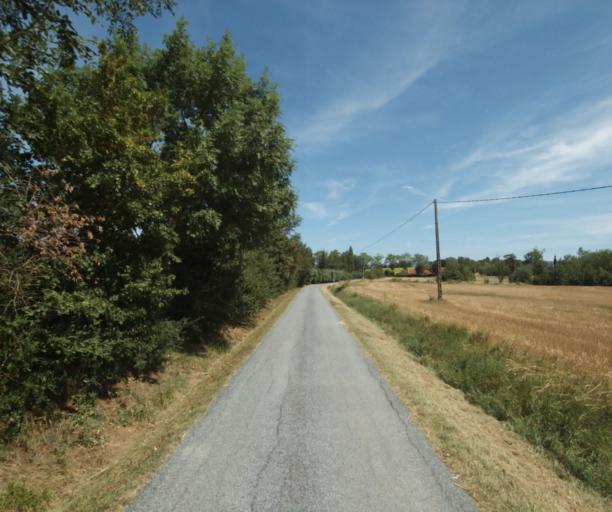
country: FR
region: Midi-Pyrenees
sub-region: Departement de la Haute-Garonne
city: Revel
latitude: 43.5061
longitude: 2.0085
